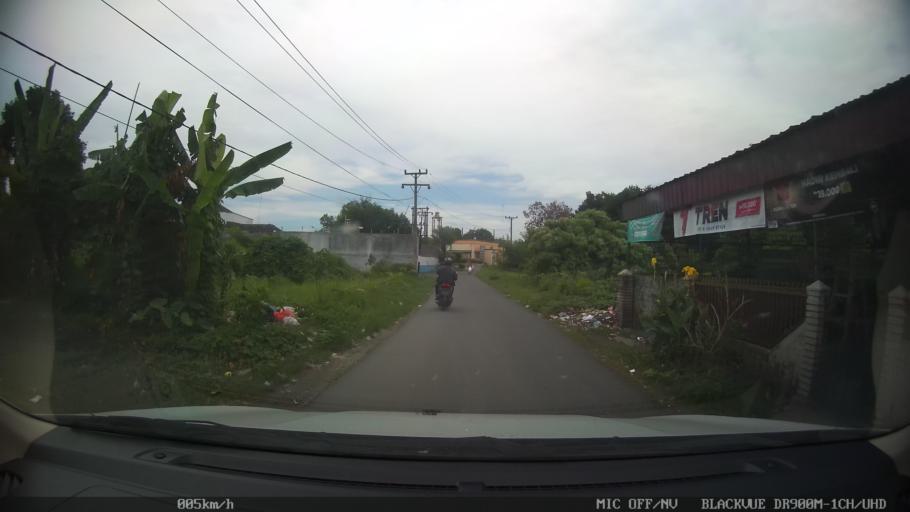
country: ID
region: North Sumatra
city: Sunggal
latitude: 3.6169
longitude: 98.6000
